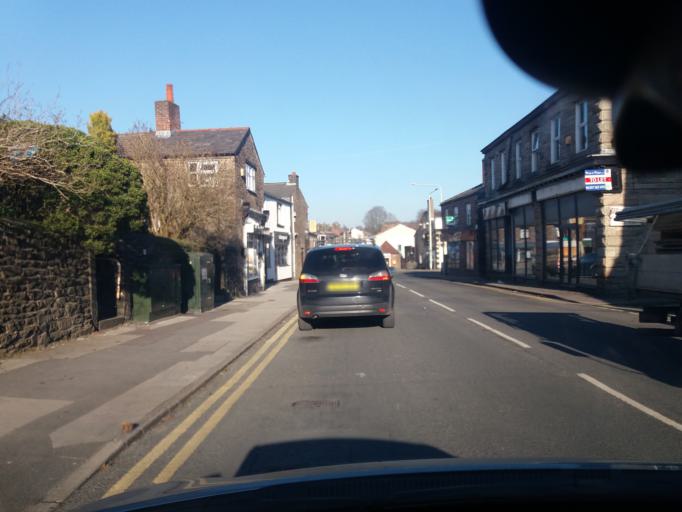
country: GB
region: England
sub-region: Lancashire
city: Adlington
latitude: 53.6168
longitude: -2.5979
